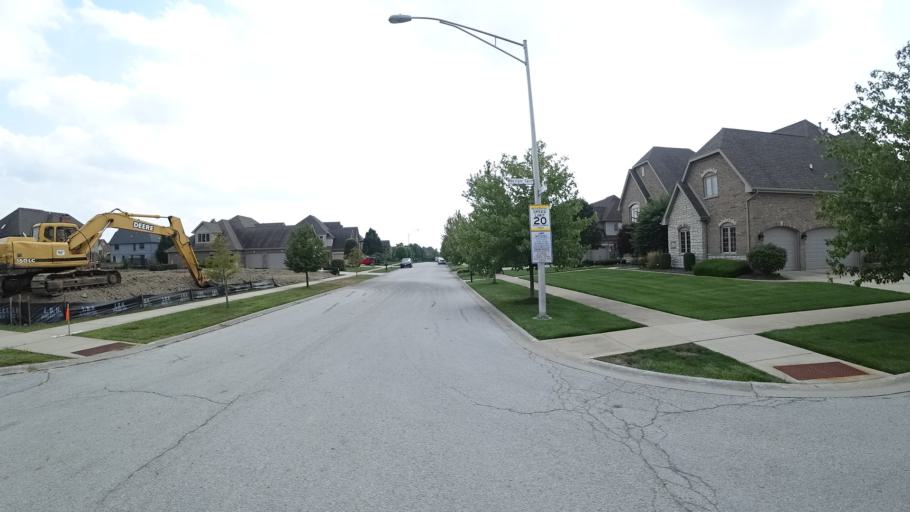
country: US
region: Illinois
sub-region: Cook County
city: Orland Park
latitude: 41.6364
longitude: -87.8896
